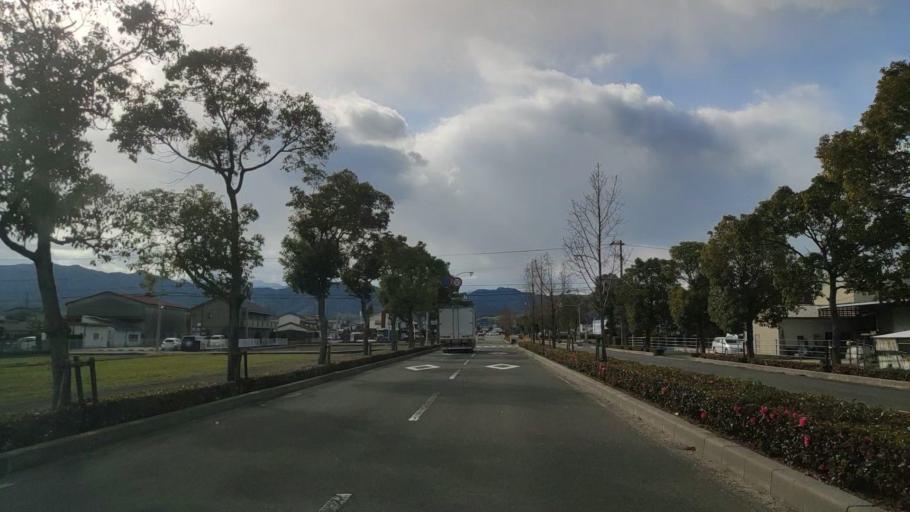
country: JP
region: Ehime
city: Saijo
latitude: 34.0396
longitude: 132.9990
